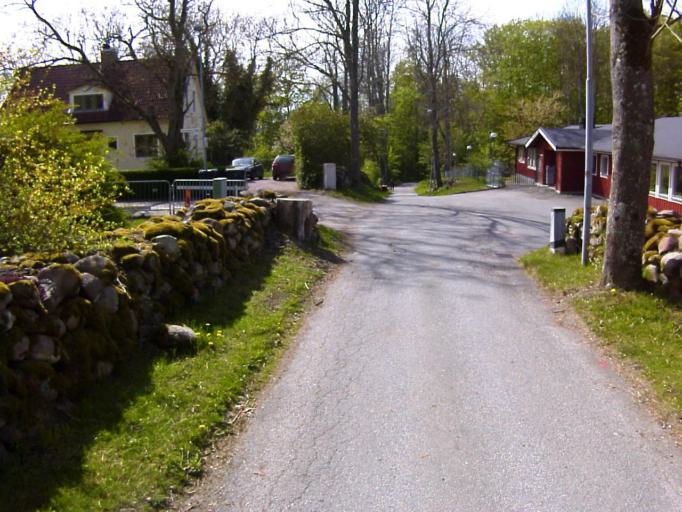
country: SE
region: Skane
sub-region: Kristianstads Kommun
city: Fjalkinge
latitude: 56.1013
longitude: 14.2482
